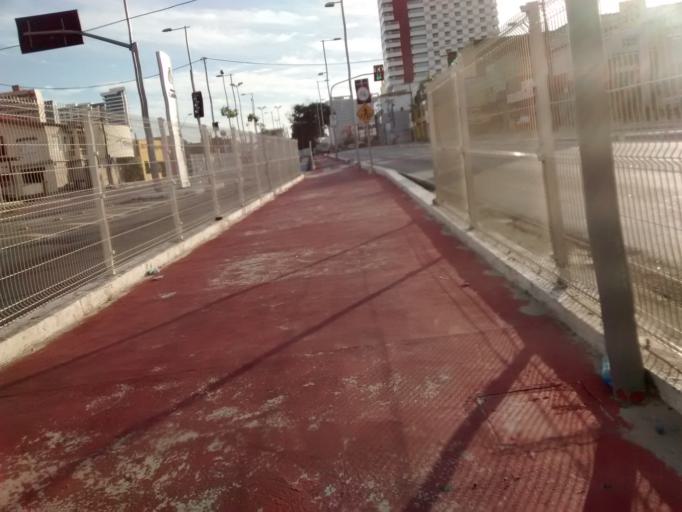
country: BR
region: Ceara
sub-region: Fortaleza
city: Fortaleza
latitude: -3.7335
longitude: -38.5538
